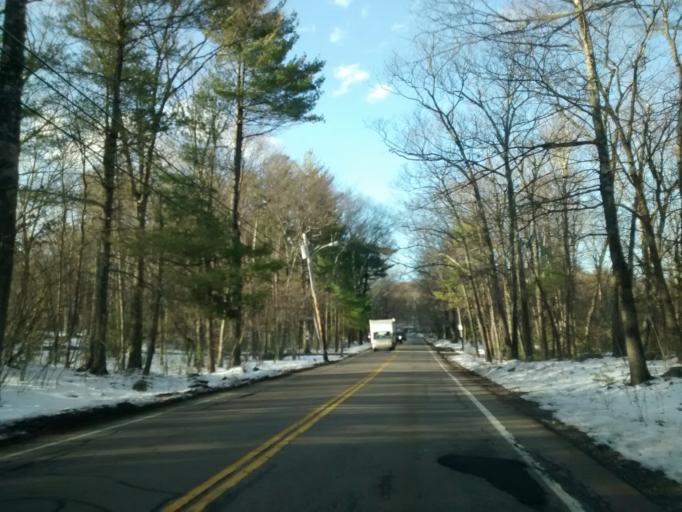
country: US
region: Massachusetts
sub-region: Middlesex County
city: Hopkinton
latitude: 42.1868
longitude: -71.5054
